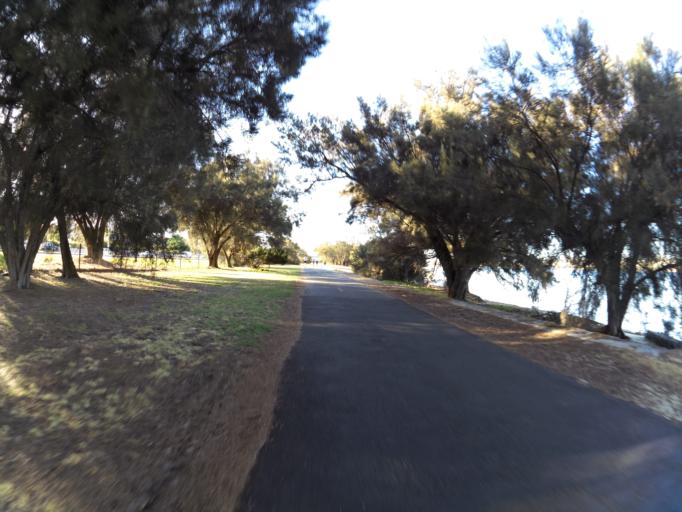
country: AU
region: Western Australia
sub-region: South Perth
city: Manning
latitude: -32.0144
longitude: 115.8571
